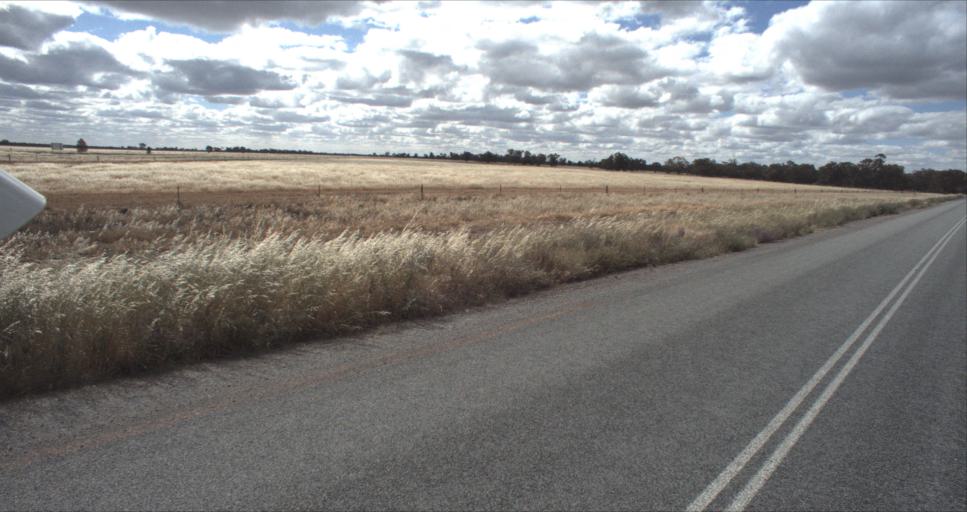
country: AU
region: New South Wales
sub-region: Leeton
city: Leeton
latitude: -34.6963
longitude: 146.3428
